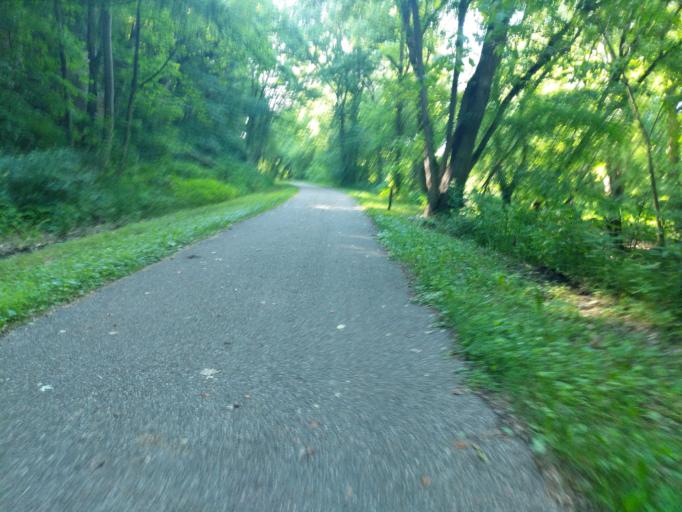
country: US
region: Ohio
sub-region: Athens County
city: Nelsonville
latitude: 39.4262
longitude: -82.1973
